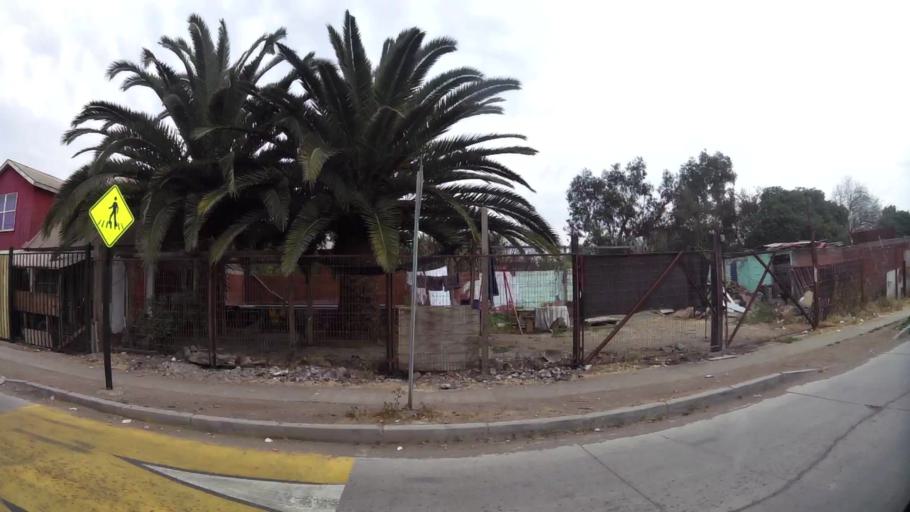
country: CL
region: Santiago Metropolitan
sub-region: Provincia de Chacabuco
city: Lampa
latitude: -33.2298
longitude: -70.8130
